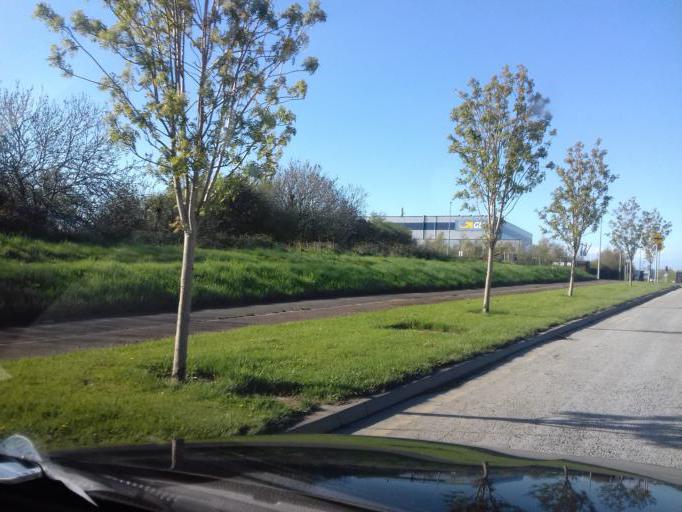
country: IE
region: Leinster
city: Castleknock
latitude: 53.3963
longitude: -6.3400
